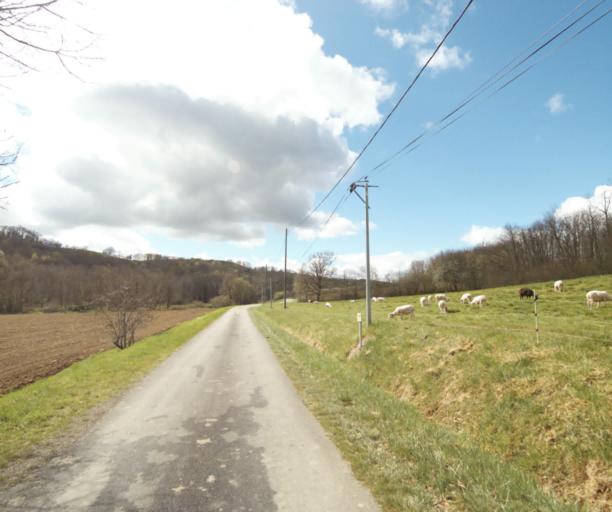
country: FR
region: Midi-Pyrenees
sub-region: Departement de l'Ariege
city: Saverdun
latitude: 43.1959
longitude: 1.5669
